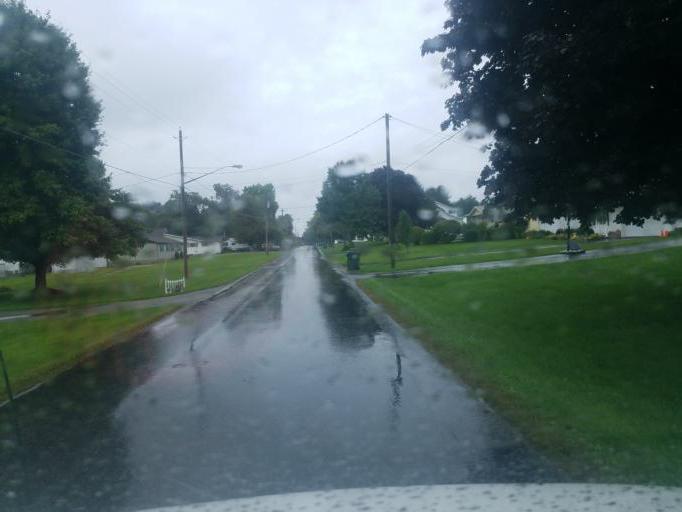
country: US
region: Ohio
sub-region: Wayne County
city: Creston
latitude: 40.9850
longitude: -81.8859
